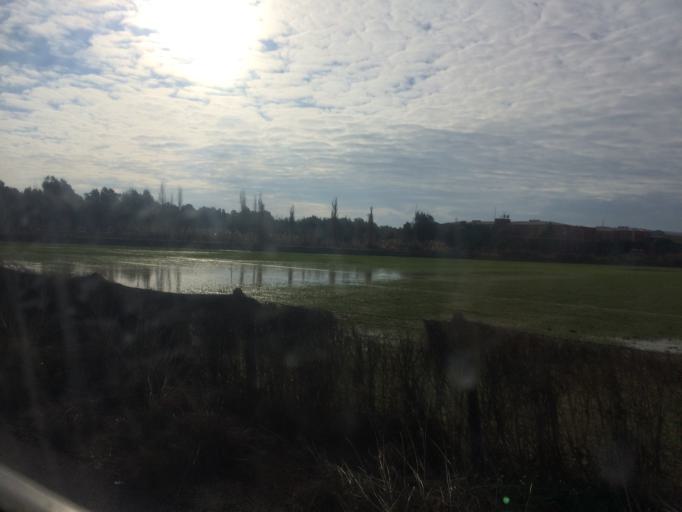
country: TR
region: Izmir
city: Karsiyaka
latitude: 38.4946
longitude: 26.9602
